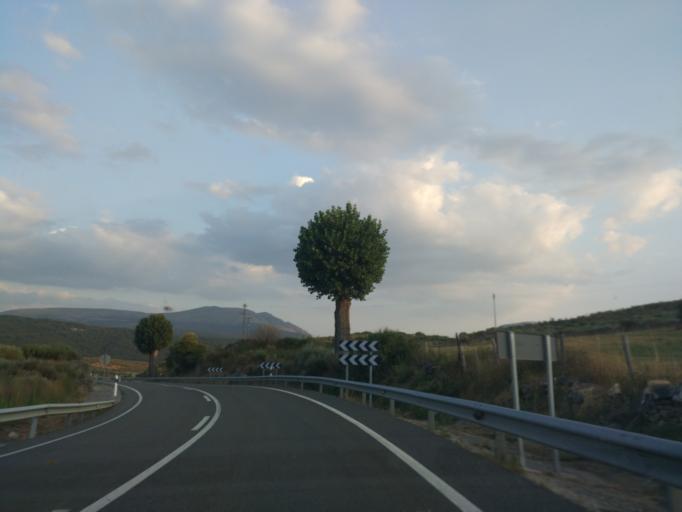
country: ES
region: Castille and Leon
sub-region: Provincia de Avila
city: San Martin del Pimpollar
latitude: 40.3809
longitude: -5.0200
